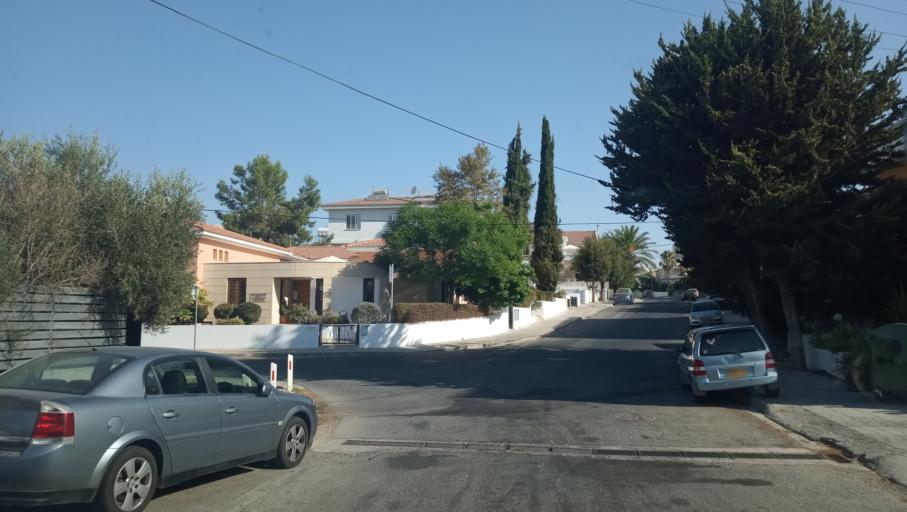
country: CY
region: Lefkosia
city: Nicosia
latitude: 35.1431
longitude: 33.3945
